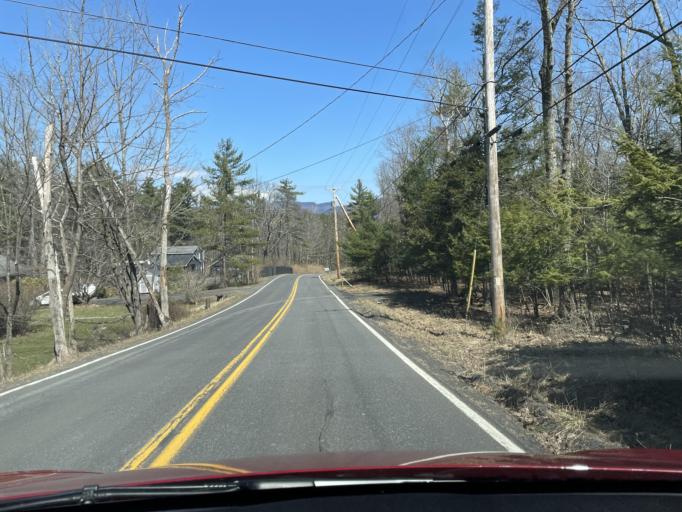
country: US
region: New York
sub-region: Ulster County
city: Woodstock
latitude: 42.0139
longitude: -74.1371
